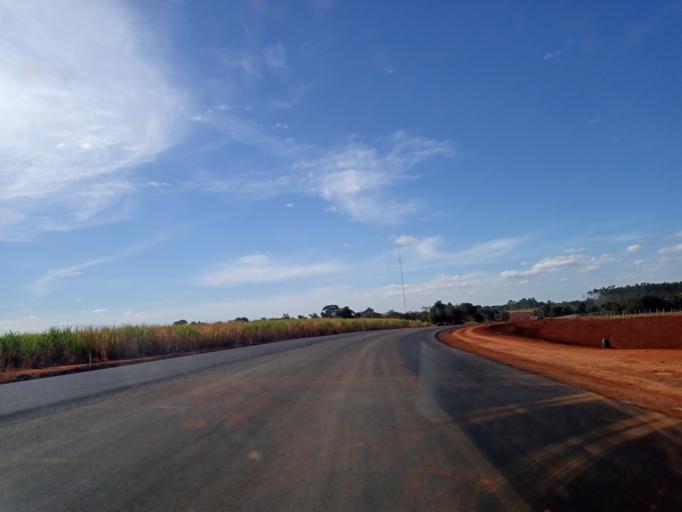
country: BR
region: Minas Gerais
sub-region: Ituiutaba
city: Ituiutaba
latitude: -18.9834
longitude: -49.5108
